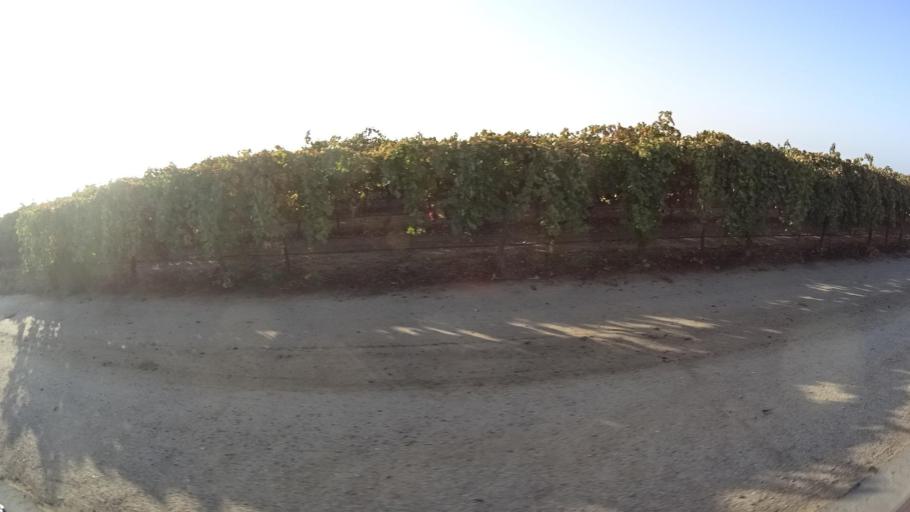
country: US
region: California
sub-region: Kern County
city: Delano
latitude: 35.7905
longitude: -119.1818
